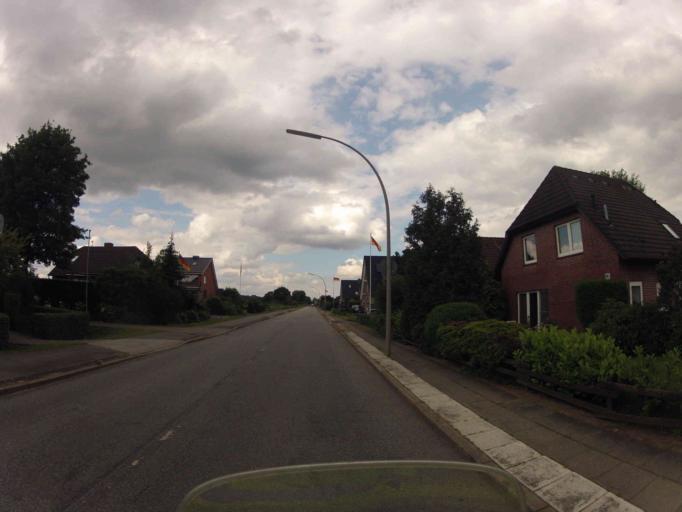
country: DE
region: Lower Saxony
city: Stelle
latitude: 53.4214
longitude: 10.1493
